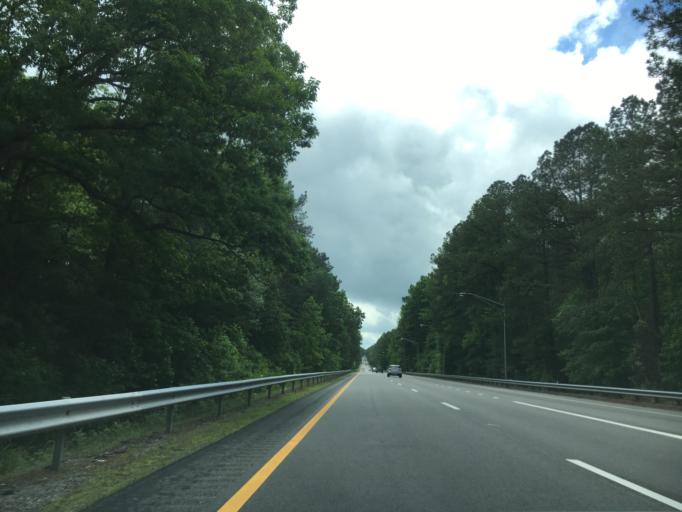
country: US
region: Virginia
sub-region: Brunswick County
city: Lawrenceville
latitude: 36.8015
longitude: -77.9875
